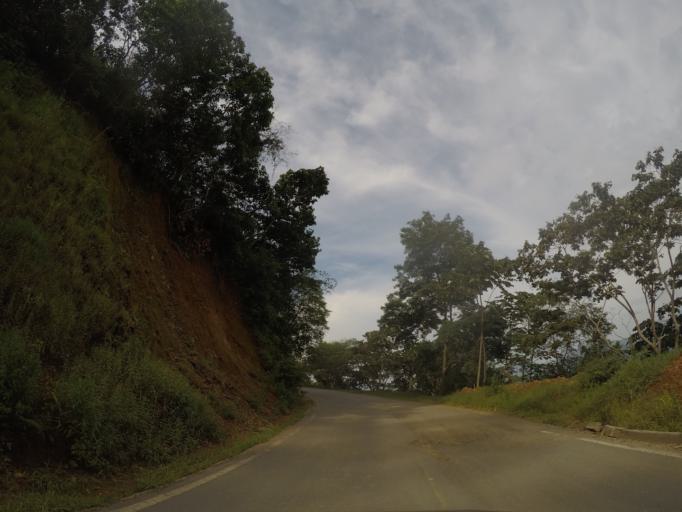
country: MX
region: Oaxaca
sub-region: San Pedro Pochutla
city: Los Naranjos Esquipulas
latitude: 15.9557
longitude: -96.4497
